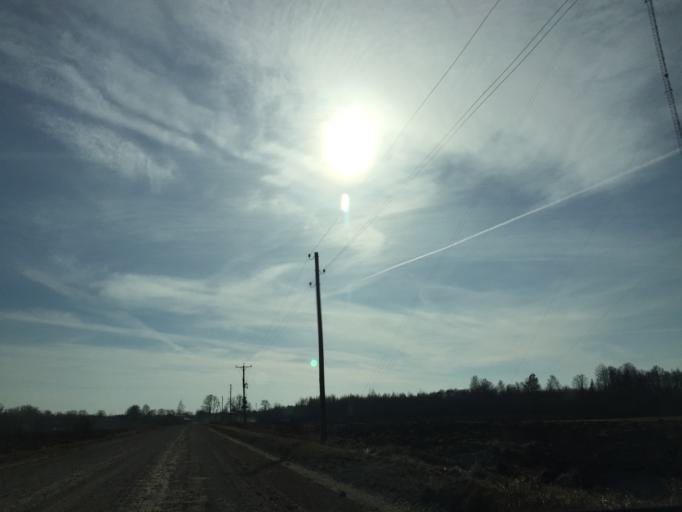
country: LV
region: Saulkrastu
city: Saulkrasti
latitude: 57.2885
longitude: 24.5113
